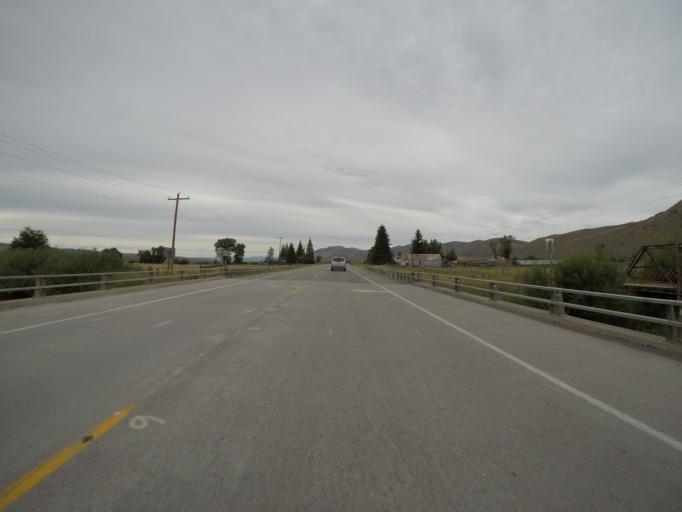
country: US
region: Idaho
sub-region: Bear Lake County
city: Montpelier
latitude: 42.0944
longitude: -110.9512
